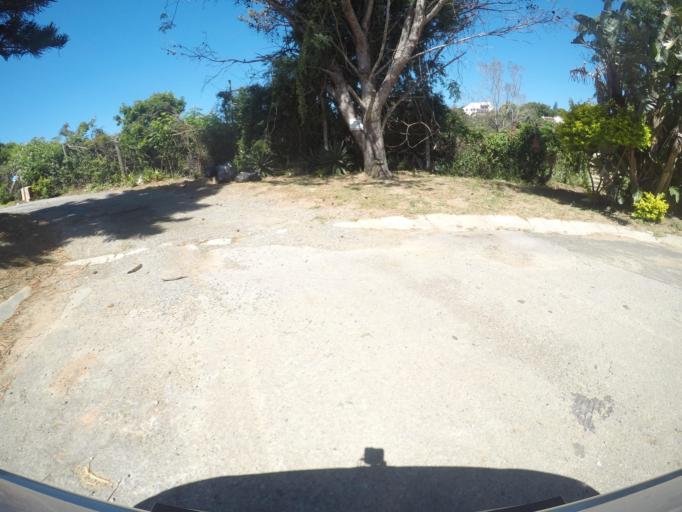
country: ZA
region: Eastern Cape
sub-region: Buffalo City Metropolitan Municipality
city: East London
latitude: -32.9750
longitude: 27.9196
